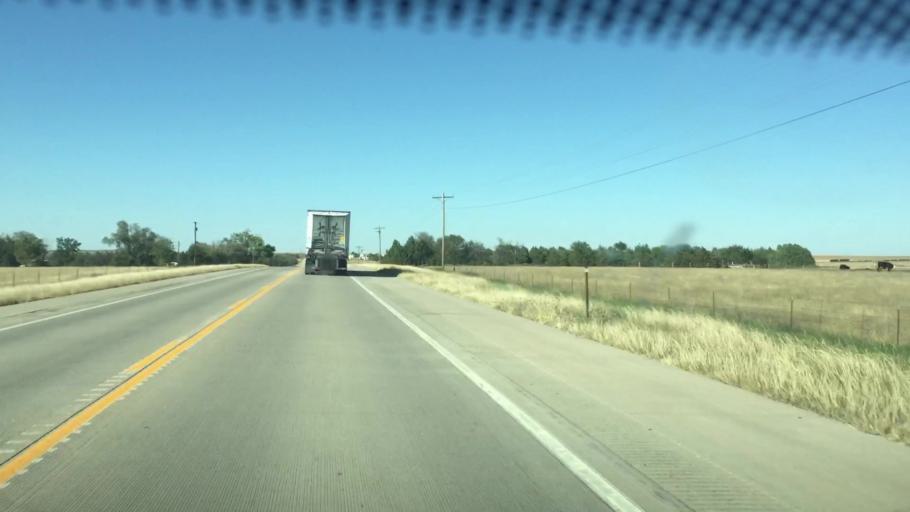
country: US
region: Colorado
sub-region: Kiowa County
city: Eads
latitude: 38.4531
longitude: -102.7306
